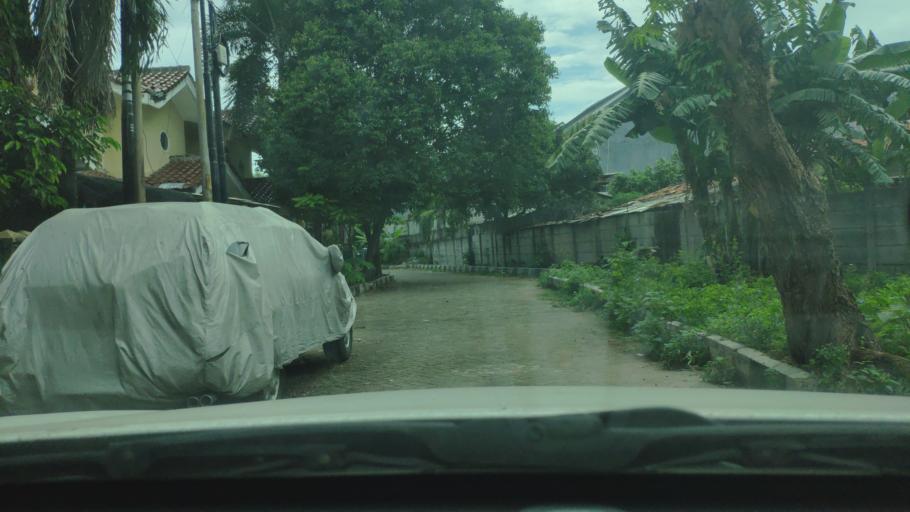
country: ID
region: West Java
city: Ciputat
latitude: -6.2202
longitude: 106.7070
